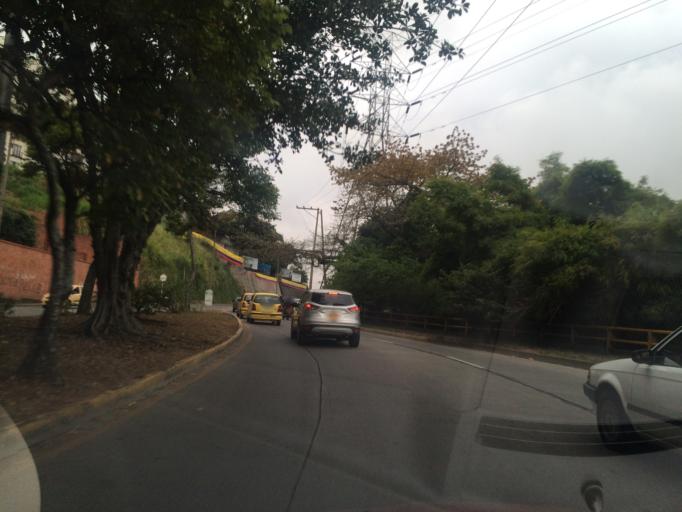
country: CO
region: Valle del Cauca
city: Cali
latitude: 3.4452
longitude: -76.5480
